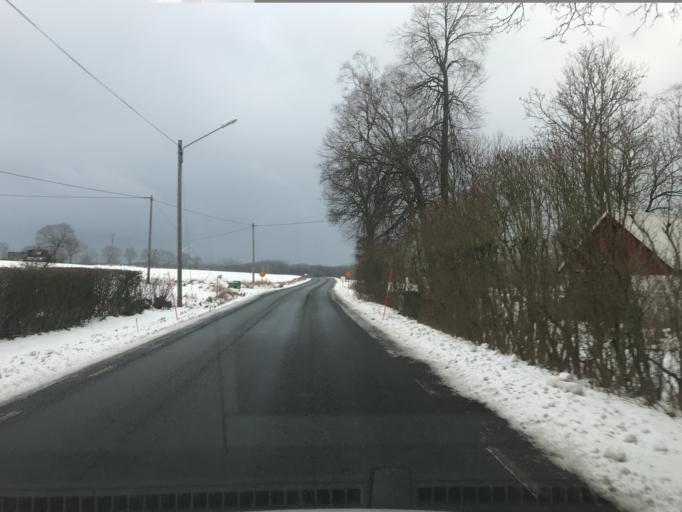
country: SE
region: Skane
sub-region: Kristianstads Kommun
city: Degeberga
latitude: 55.7433
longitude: 13.9402
